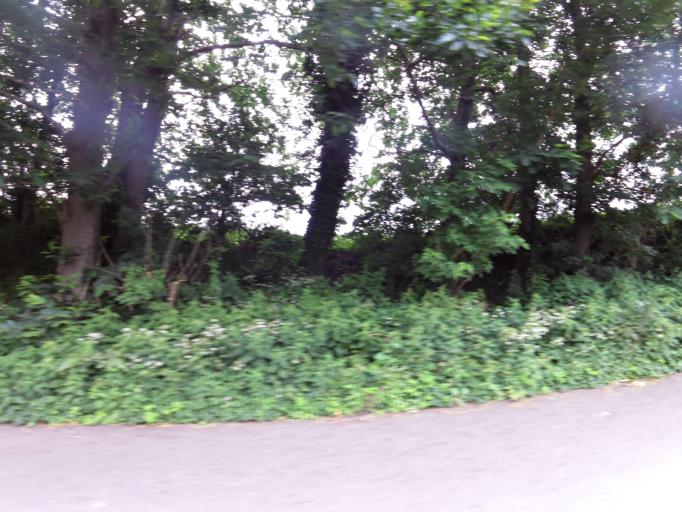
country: FR
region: Nord-Pas-de-Calais
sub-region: Departement du Nord
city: Steenwerck
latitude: 50.7709
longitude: 2.8001
